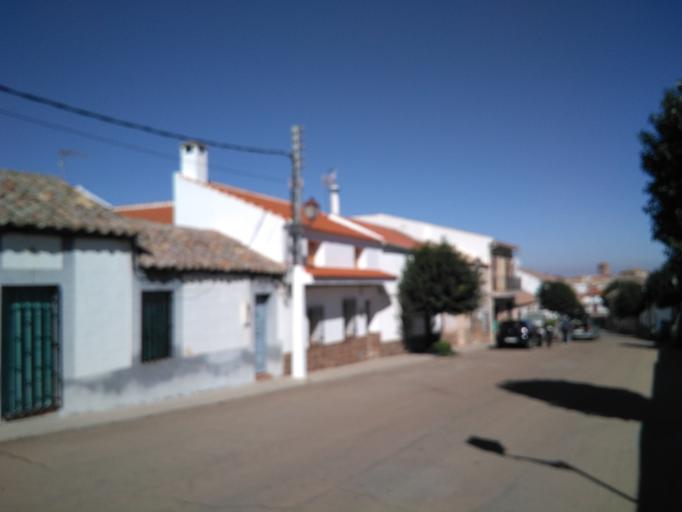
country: ES
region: Castille-La Mancha
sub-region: Provincia de Ciudad Real
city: Ballesteros de Calatrava
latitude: 38.8336
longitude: -3.9459
